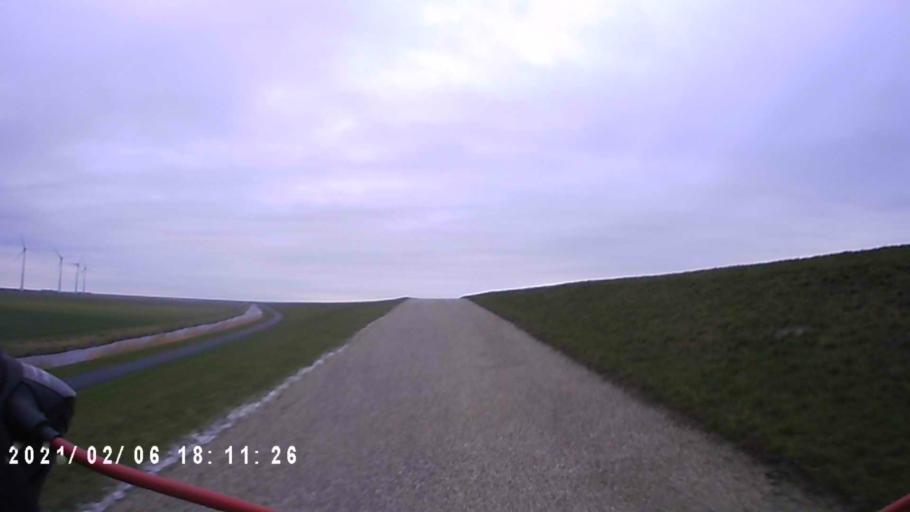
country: DE
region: Lower Saxony
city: Borkum
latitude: 53.4594
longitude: 6.7815
